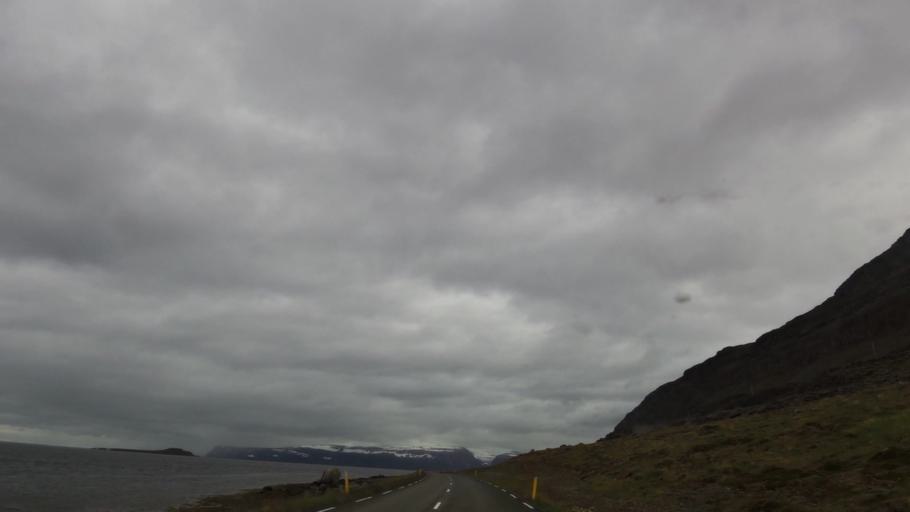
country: IS
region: Westfjords
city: Isafjoerdur
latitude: 66.0138
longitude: -22.7816
